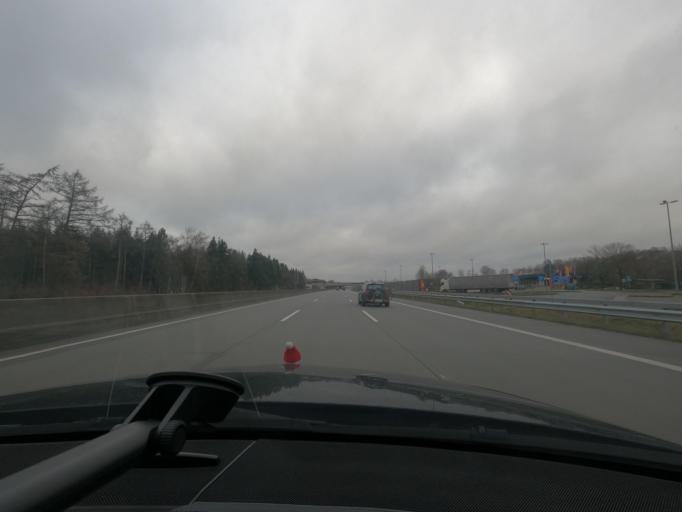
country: DE
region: Schleswig-Holstein
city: Padenstedt
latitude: 54.0123
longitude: 9.9319
